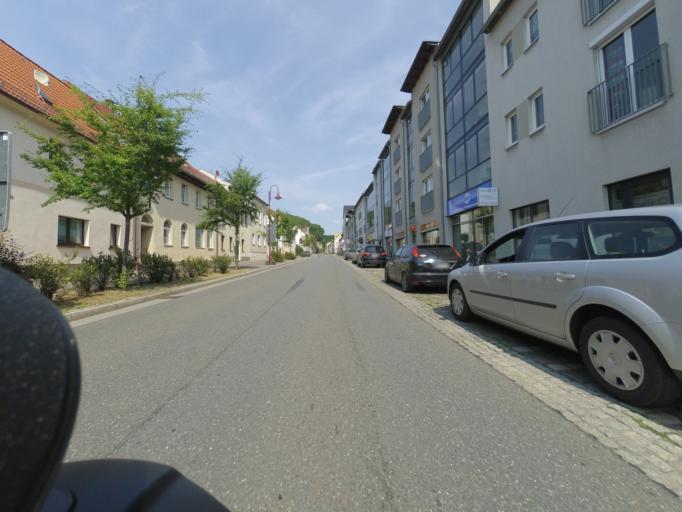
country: DE
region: Thuringia
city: Bad Kostritz
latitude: 50.9214
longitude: 12.0571
